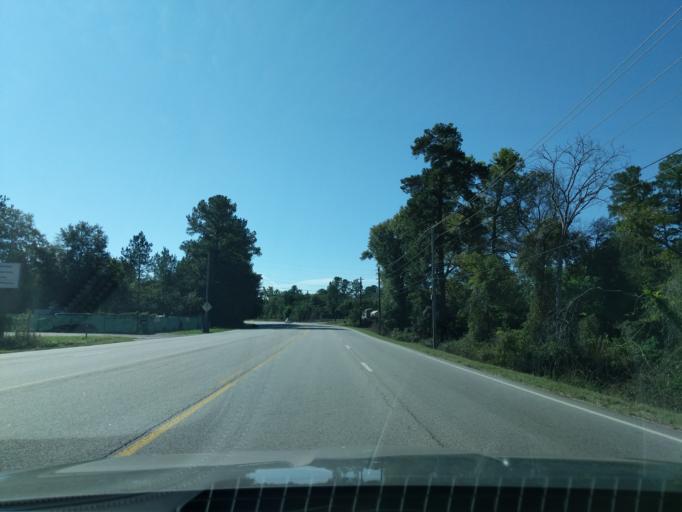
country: US
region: Georgia
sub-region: Richmond County
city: Augusta
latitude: 33.4212
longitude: -82.0069
